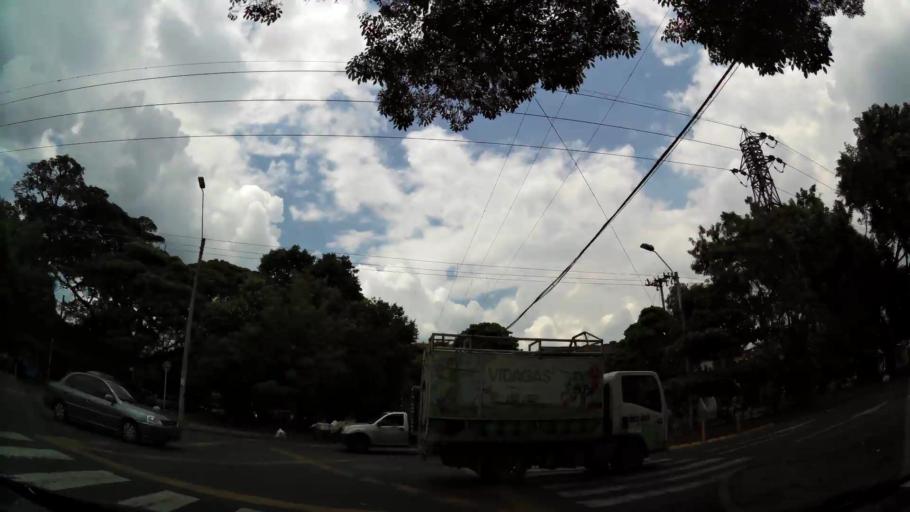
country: CO
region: Valle del Cauca
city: Cali
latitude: 3.4666
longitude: -76.4978
